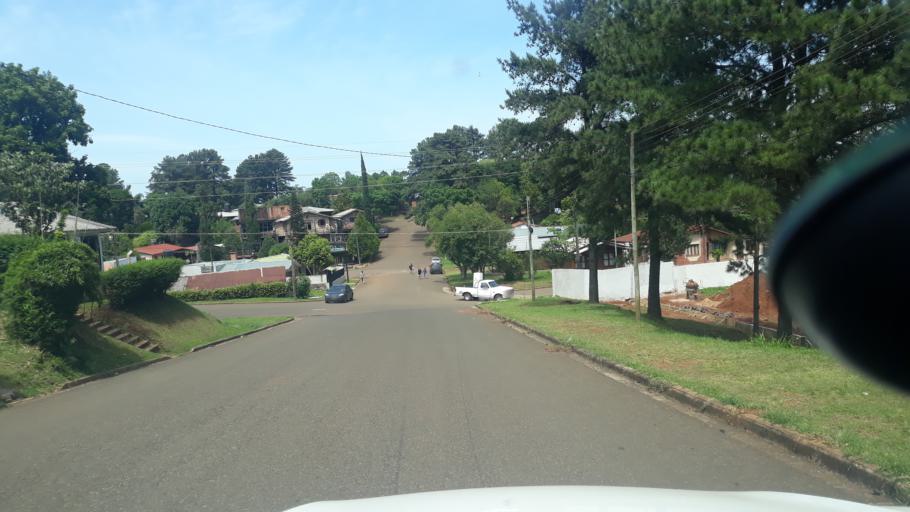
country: AR
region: Misiones
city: Bernardo de Irigoyen
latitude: -26.2523
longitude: -53.6484
